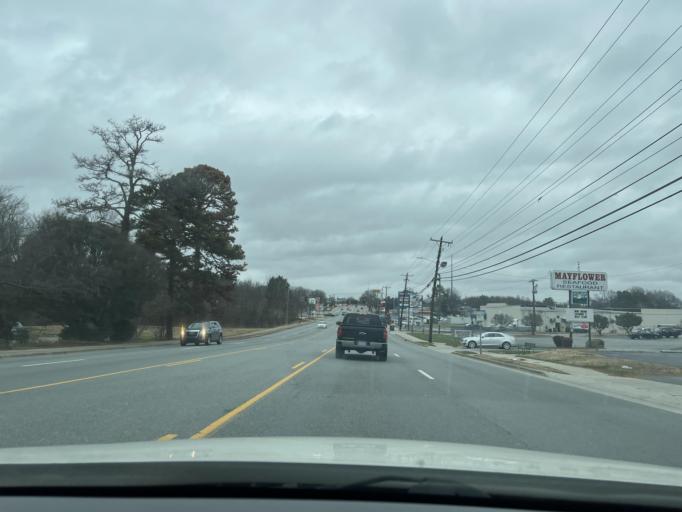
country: US
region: North Carolina
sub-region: Guilford County
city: Greensboro
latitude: 36.0278
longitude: -79.8021
